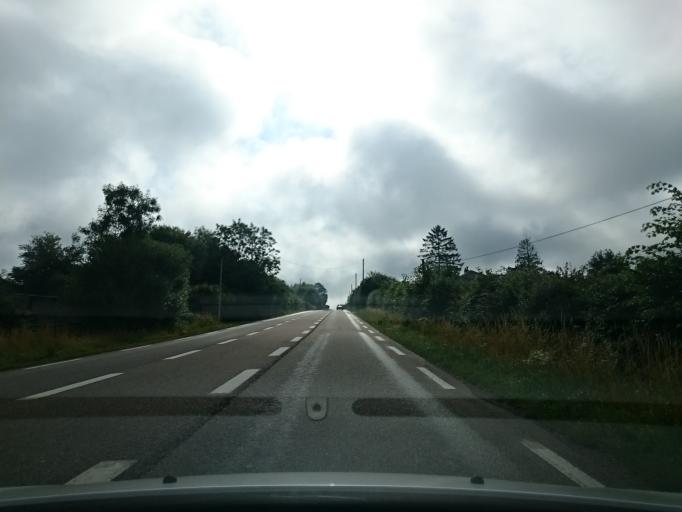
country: FR
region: Lower Normandy
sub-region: Departement du Calvados
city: Saint-Desir
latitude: 49.1353
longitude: 0.1395
